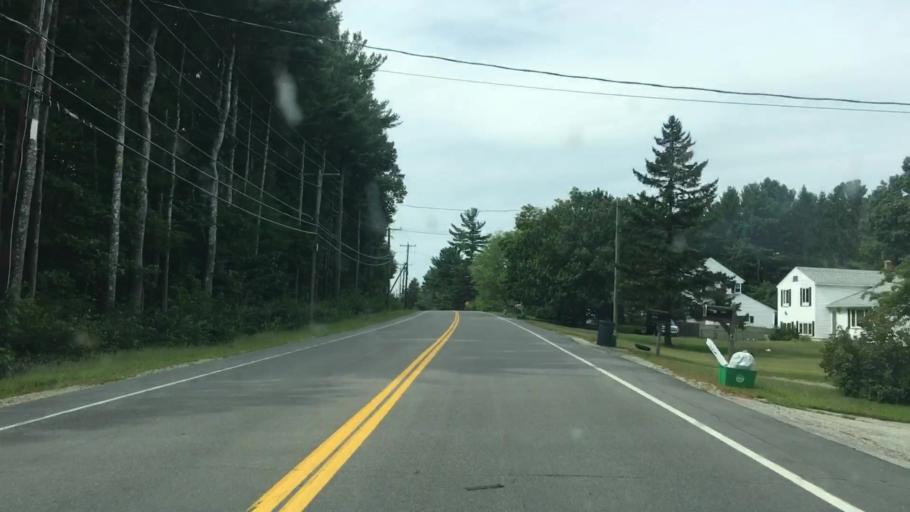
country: US
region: New Hampshire
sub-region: Strafford County
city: Madbury
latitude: 43.1920
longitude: -70.9282
